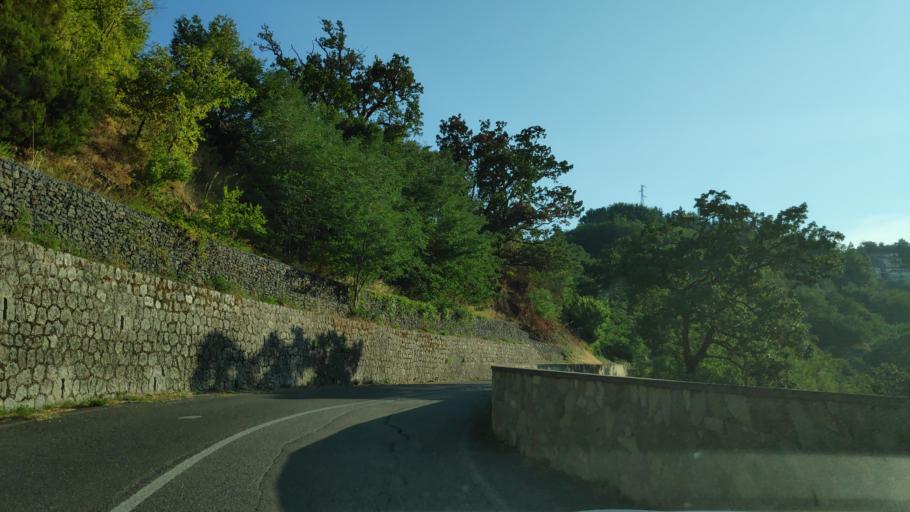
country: IT
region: Calabria
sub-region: Provincia di Catanzaro
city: Satriano
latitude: 38.6714
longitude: 16.4877
